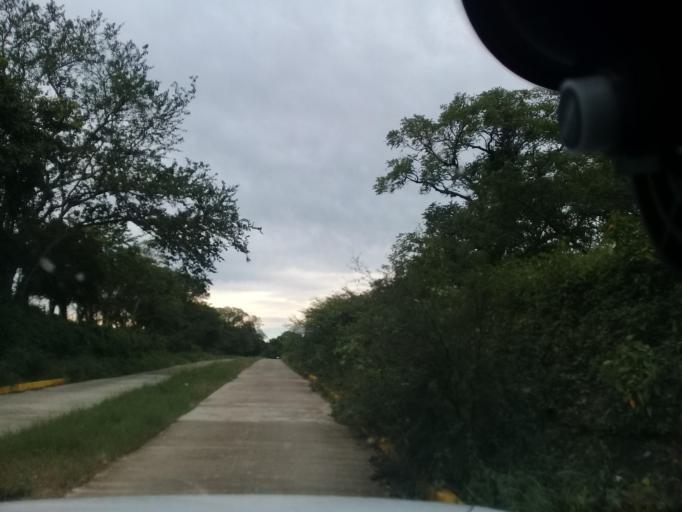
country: MX
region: Hidalgo
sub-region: Huejutla de Reyes
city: Chalahuiyapa
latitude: 21.1626
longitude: -98.3595
